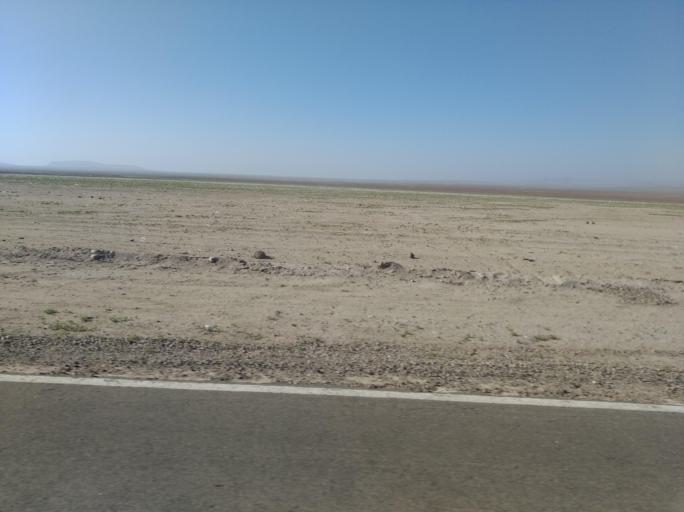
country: CL
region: Atacama
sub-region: Provincia de Copiapo
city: Copiapo
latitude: -27.3164
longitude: -70.8688
